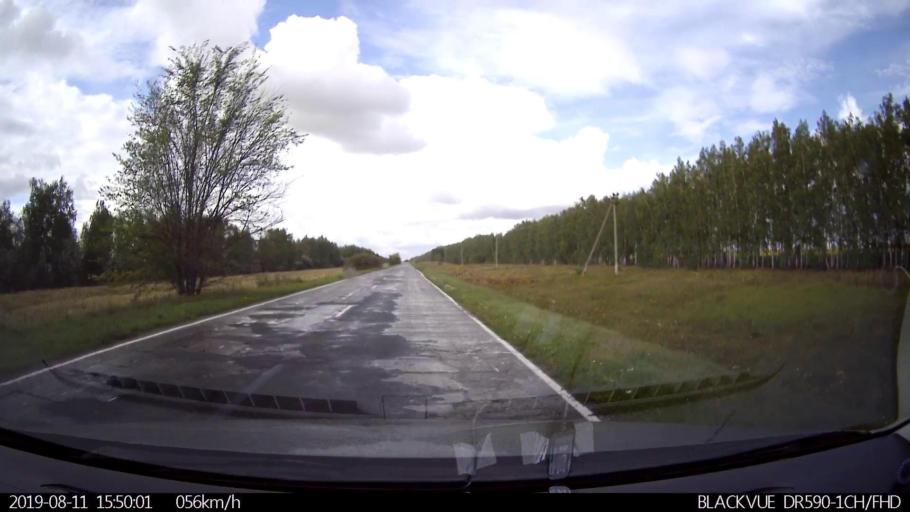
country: RU
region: Ulyanovsk
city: Ignatovka
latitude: 53.9090
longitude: 47.6557
